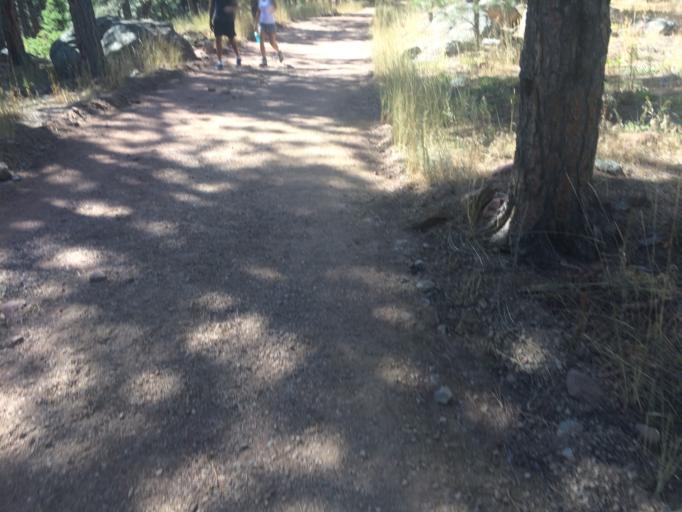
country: US
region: Colorado
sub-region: Boulder County
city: Boulder
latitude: 39.9645
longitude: -105.2779
